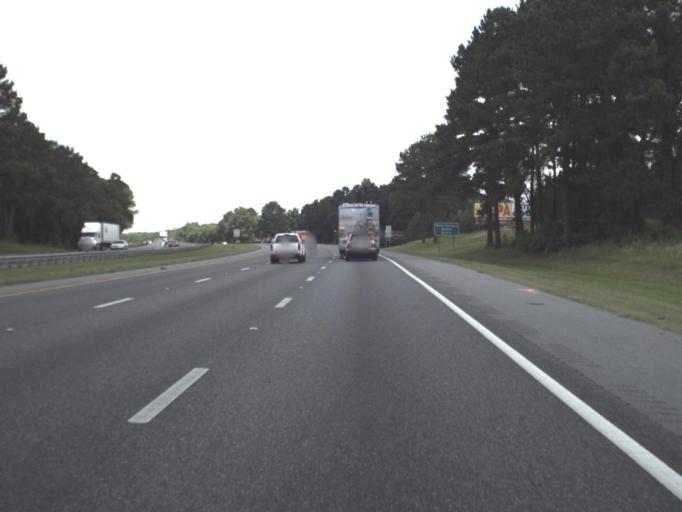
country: US
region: Florida
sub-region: Suwannee County
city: Wellborn
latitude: 30.2751
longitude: -82.7589
